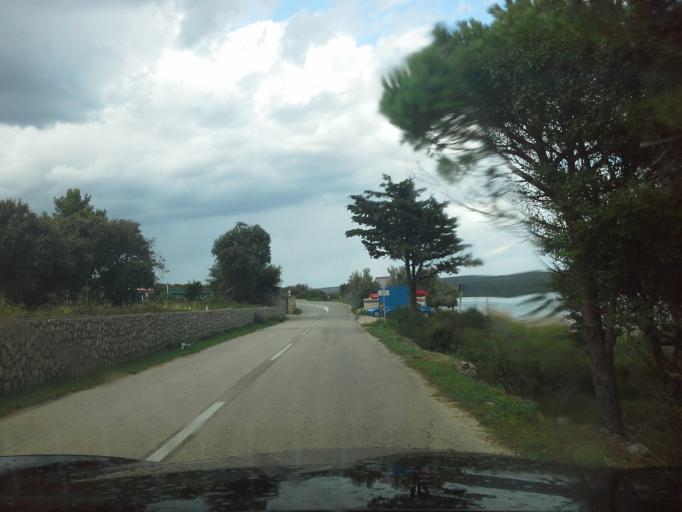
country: HR
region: Primorsko-Goranska
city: Mali Losinj
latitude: 44.6667
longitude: 14.3970
